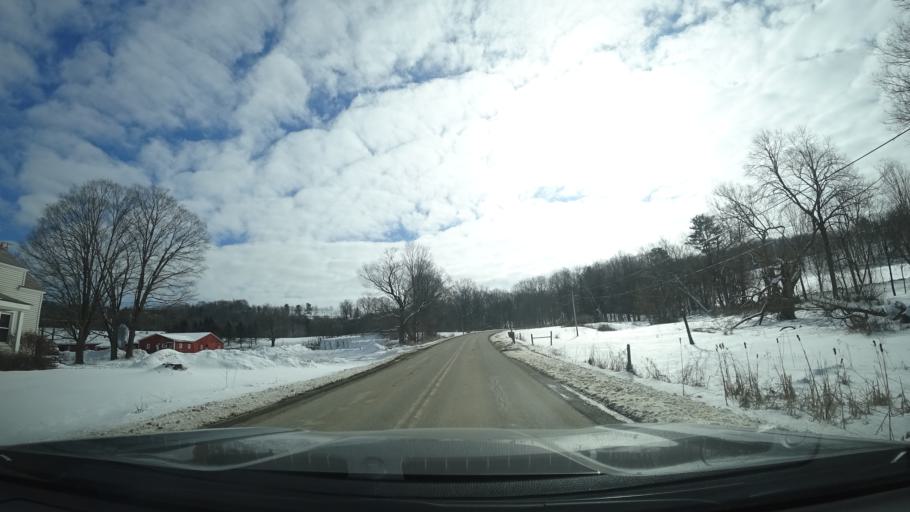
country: US
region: New York
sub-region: Washington County
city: Fort Edward
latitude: 43.2453
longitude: -73.4502
